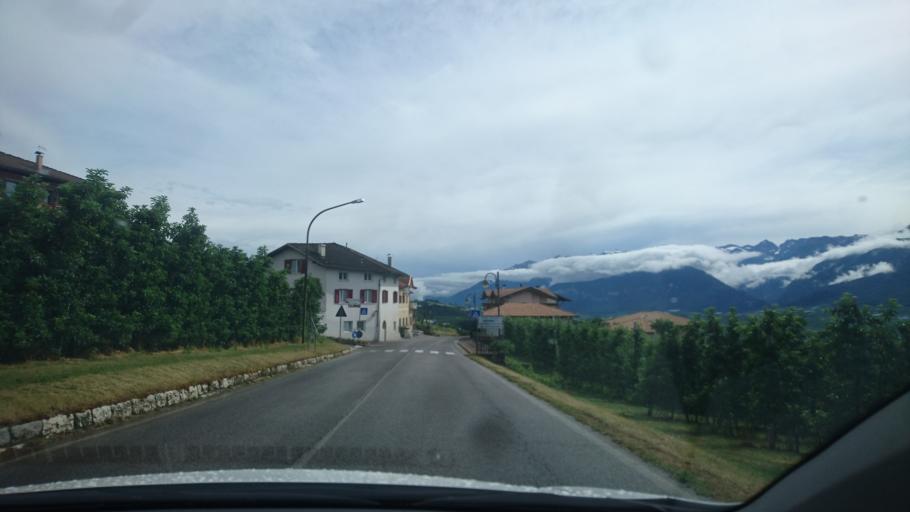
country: IT
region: Trentino-Alto Adige
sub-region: Provincia di Trento
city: Sanzeno
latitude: 46.3795
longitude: 11.0893
